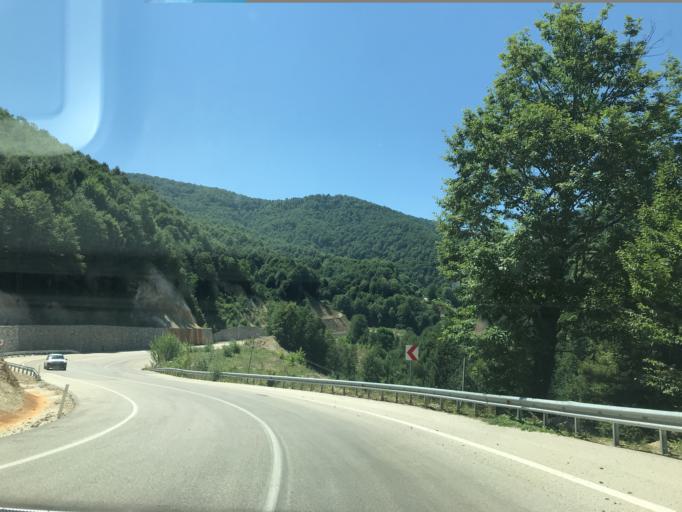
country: TR
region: Bursa
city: Tahtakopru
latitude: 39.9363
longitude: 29.5887
